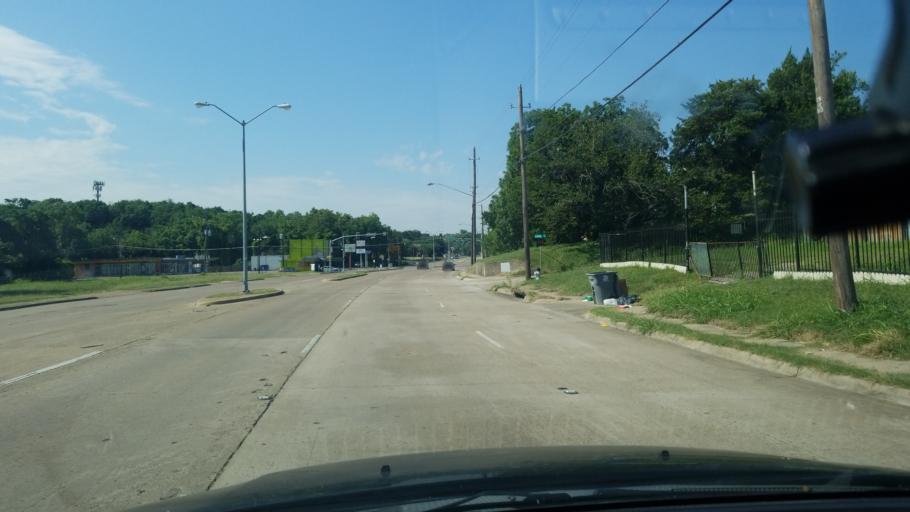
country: US
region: Texas
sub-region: Dallas County
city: Dallas
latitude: 32.7405
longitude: -96.7985
